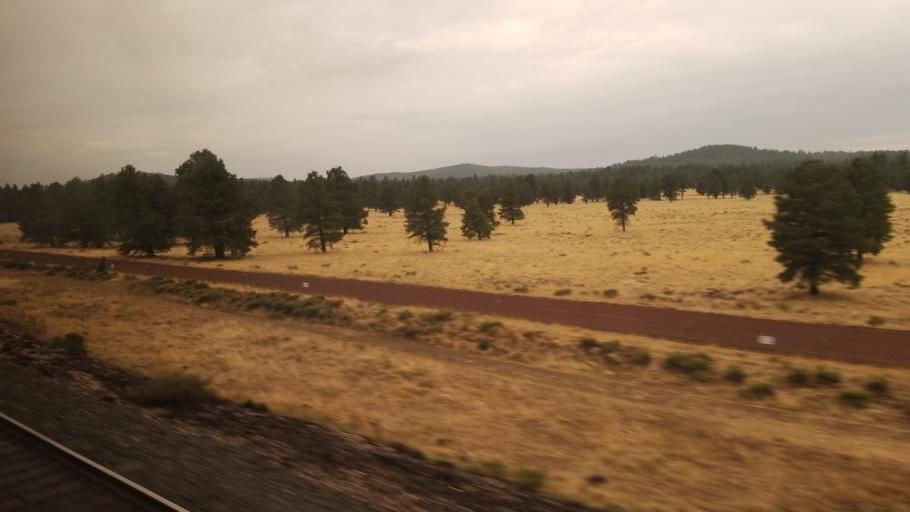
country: US
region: Arizona
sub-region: Coconino County
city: Flagstaff
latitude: 35.2228
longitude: -111.7992
